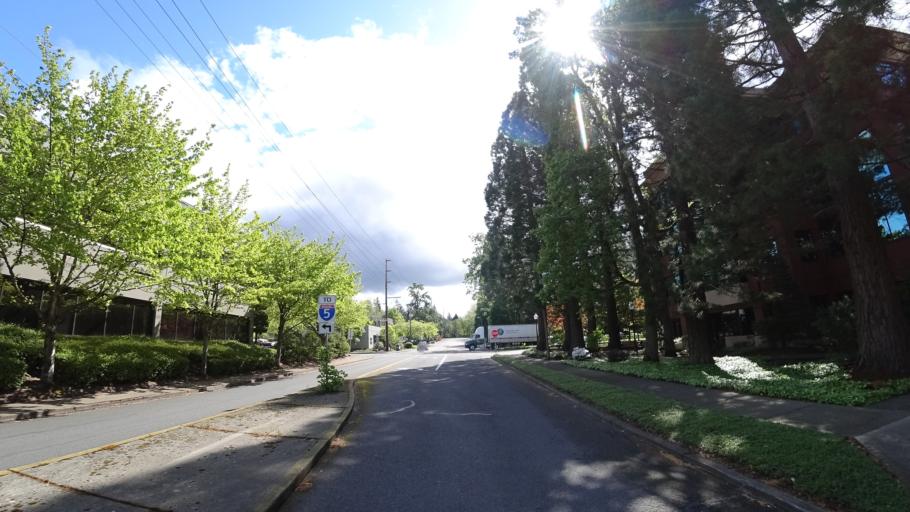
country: US
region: Oregon
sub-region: Washington County
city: Metzger
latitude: 45.4275
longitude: -122.7477
